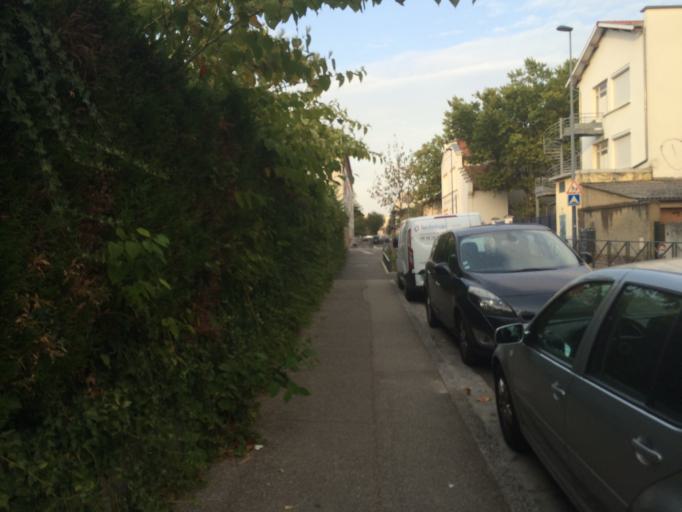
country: FR
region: Rhone-Alpes
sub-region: Departement du Rhone
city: Villeurbanne
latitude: 45.7786
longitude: 4.8844
